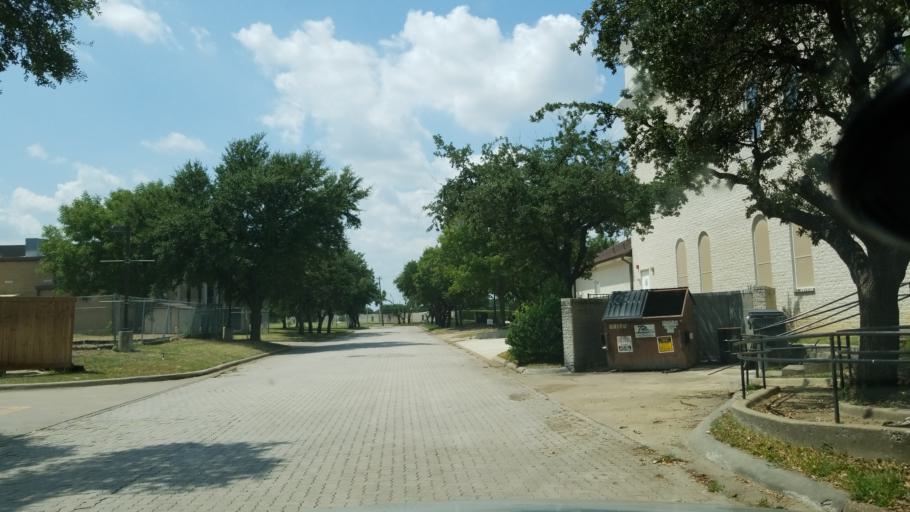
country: US
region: Texas
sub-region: Dallas County
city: Richardson
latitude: 32.9264
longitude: -96.7342
